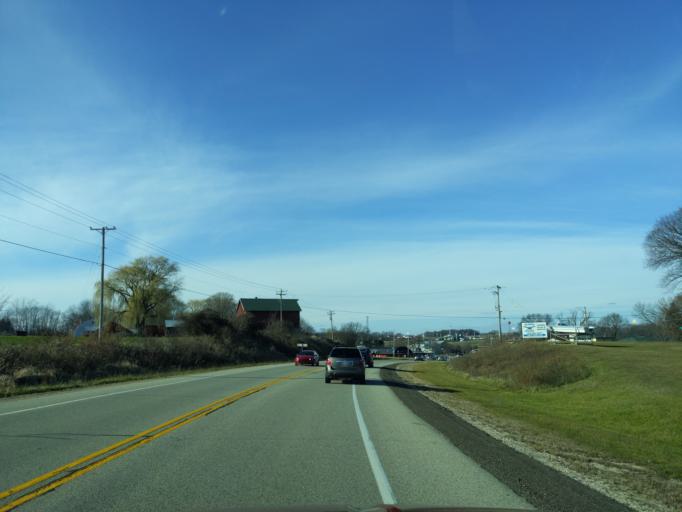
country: US
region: Wisconsin
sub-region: Rock County
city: Edgerton
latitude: 42.8275
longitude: -89.0184
